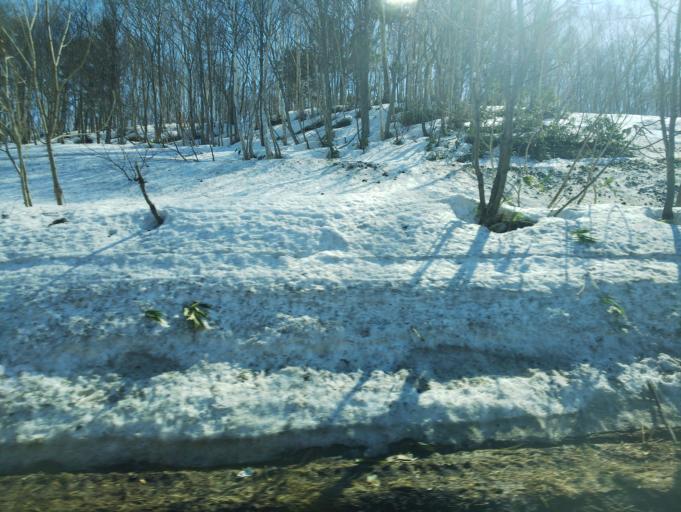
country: JP
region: Hokkaido
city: Nayoro
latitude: 44.7022
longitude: 142.2736
